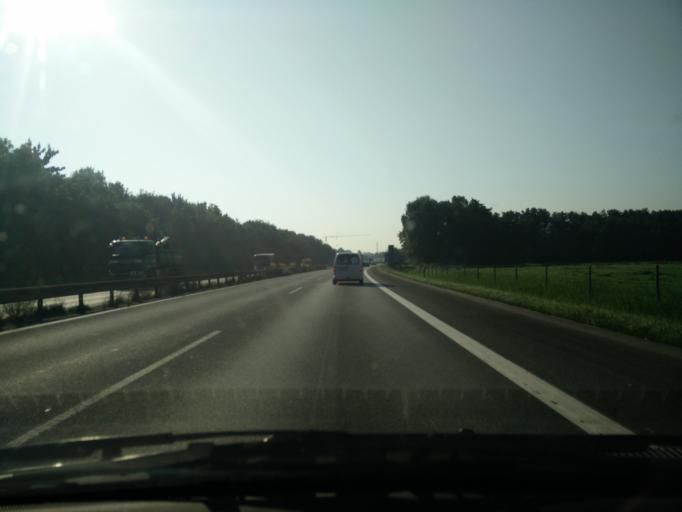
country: DE
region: Schleswig-Holstein
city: Rellingen
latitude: 53.6461
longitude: 9.8290
